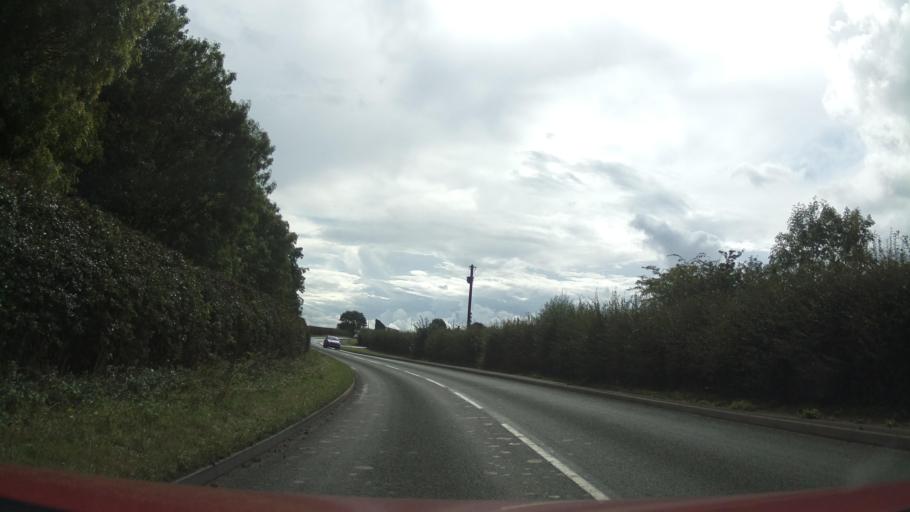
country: GB
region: England
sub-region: Staffordshire
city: Eccleshall
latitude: 52.8824
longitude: -2.2352
